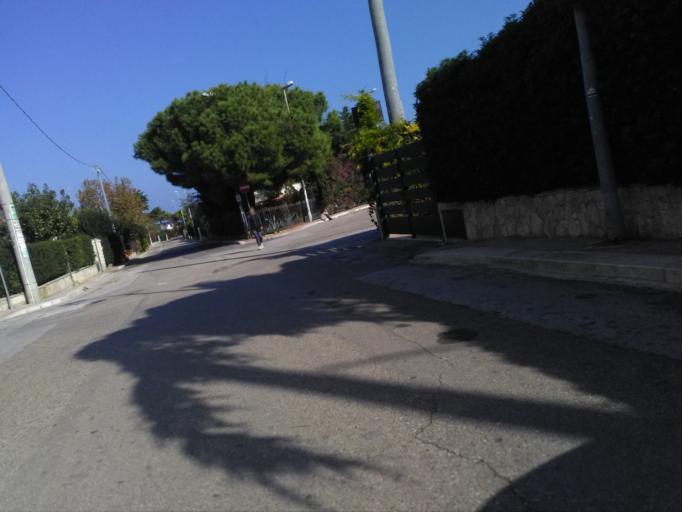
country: IT
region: Apulia
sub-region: Provincia di Bari
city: San Paolo
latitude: 41.1577
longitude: 16.7680
